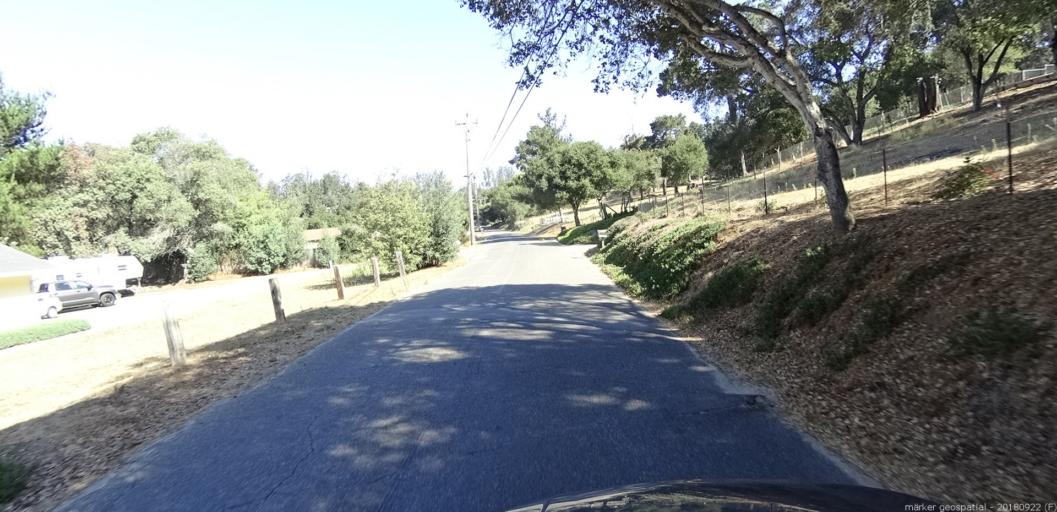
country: US
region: California
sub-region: Monterey County
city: Prunedale
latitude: 36.8145
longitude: -121.6621
